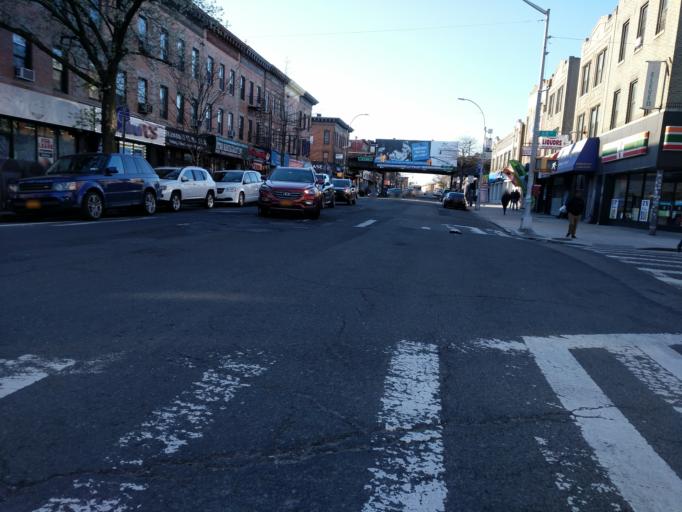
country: US
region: New York
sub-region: Kings County
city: East New York
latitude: 40.7051
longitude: -73.8962
